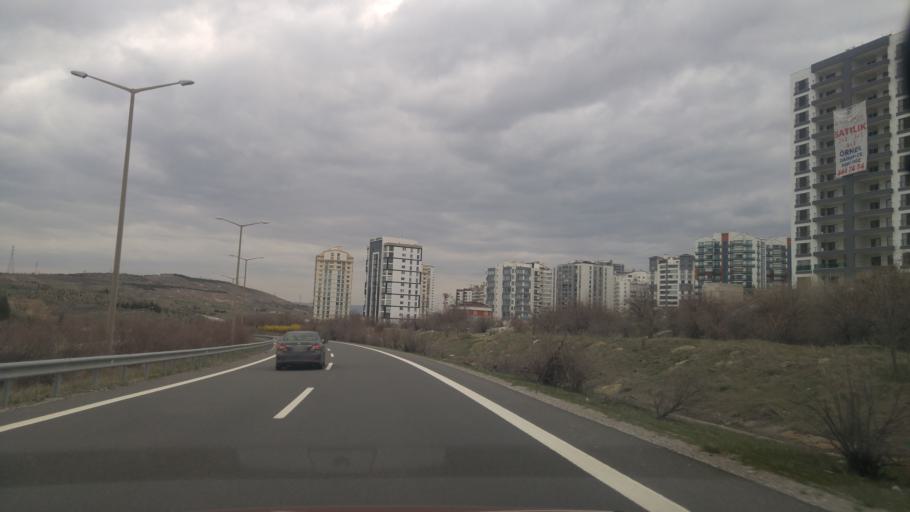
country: TR
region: Ankara
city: Etimesgut
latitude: 39.8595
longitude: 32.6304
